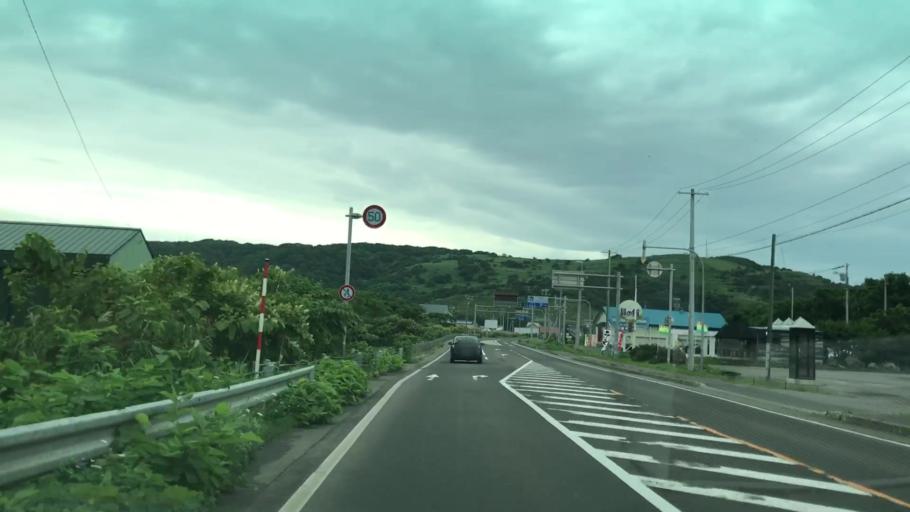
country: JP
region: Hokkaido
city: Iwanai
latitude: 42.8808
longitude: 140.3712
